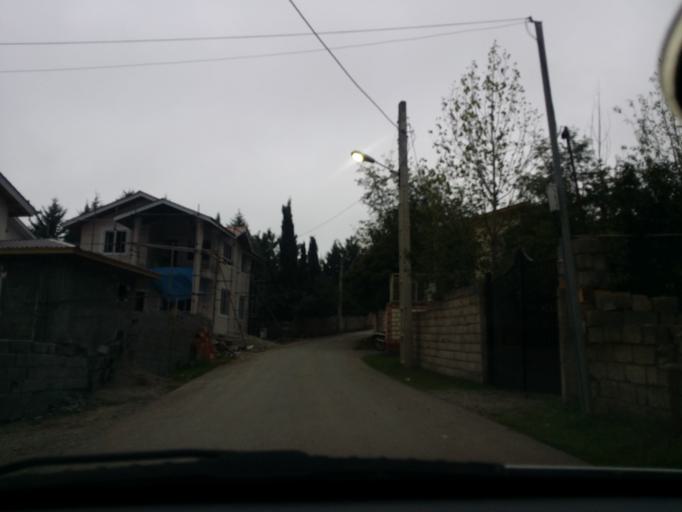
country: IR
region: Mazandaran
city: Chalus
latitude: 36.5096
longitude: 51.2292
